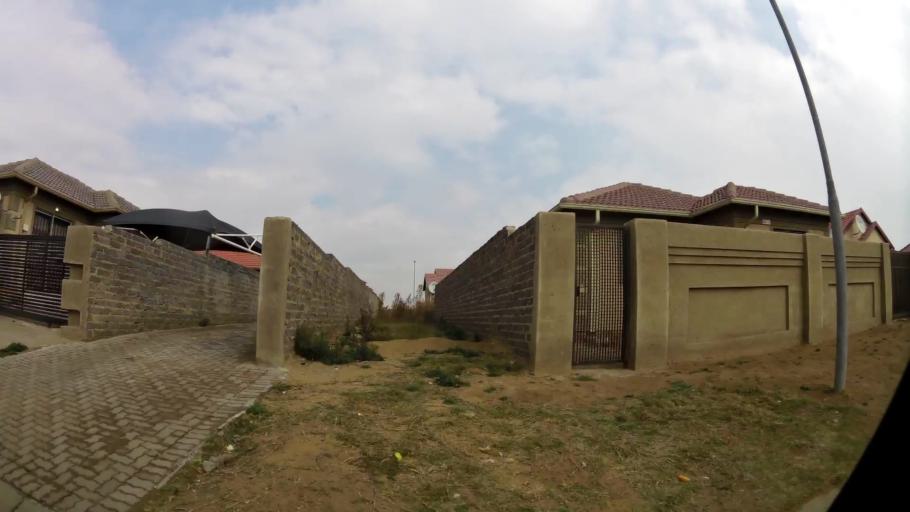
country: ZA
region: Gauteng
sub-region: Sedibeng District Municipality
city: Vanderbijlpark
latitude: -26.6816
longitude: 27.8436
